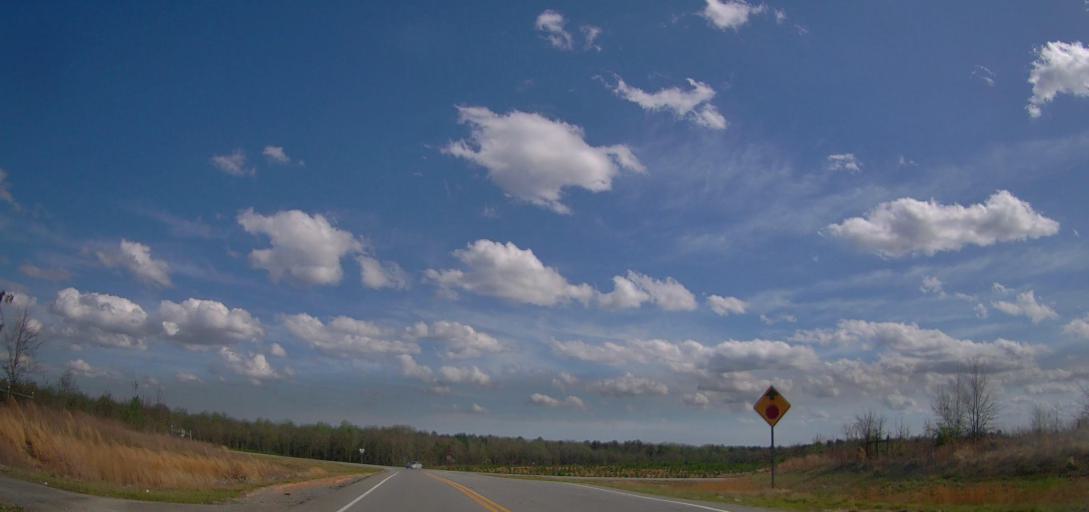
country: US
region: Georgia
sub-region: Wilkinson County
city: Gordon
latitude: 32.9401
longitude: -83.2883
